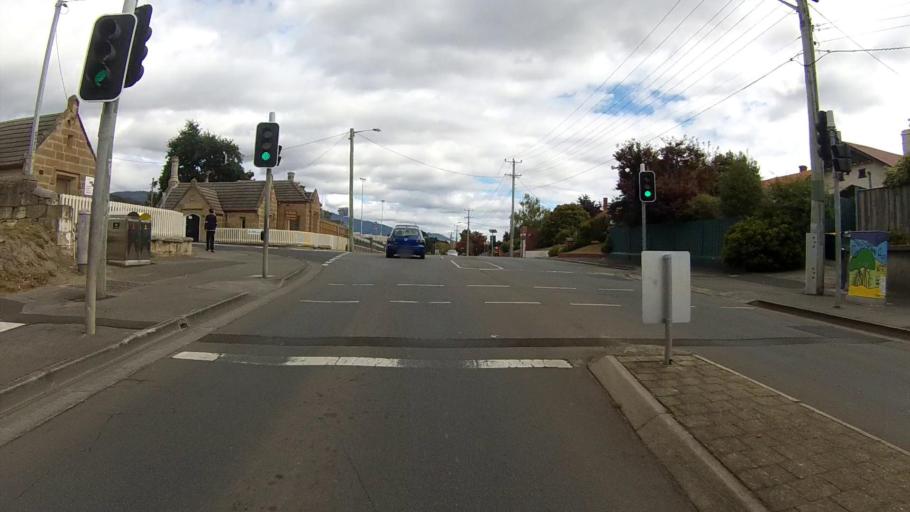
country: AU
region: Tasmania
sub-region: Glenorchy
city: Moonah
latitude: -42.8535
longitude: 147.3007
